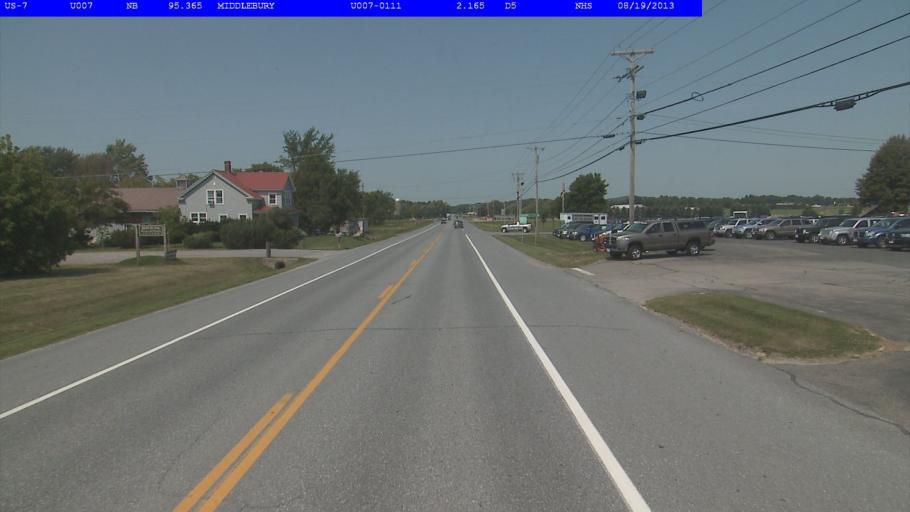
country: US
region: Vermont
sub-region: Addison County
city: Middlebury (village)
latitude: 43.9837
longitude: -73.1288
